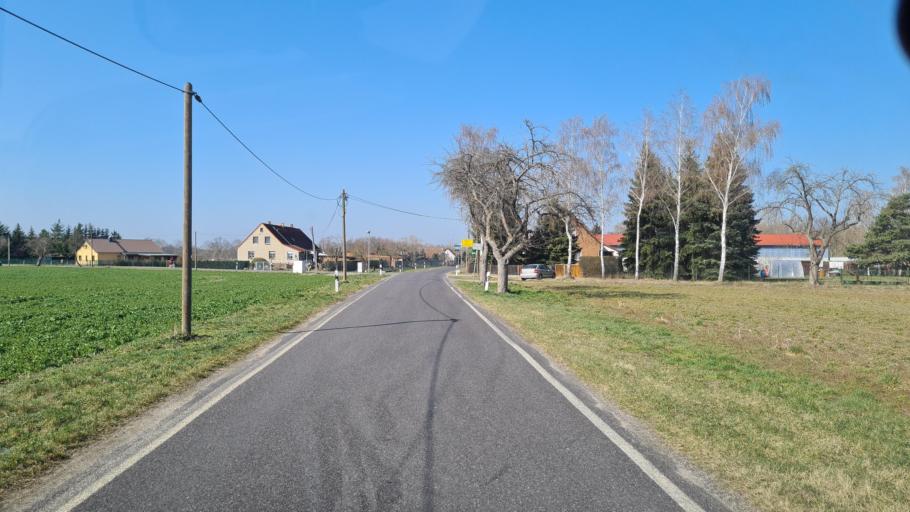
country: DE
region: Brandenburg
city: Vetschau
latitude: 51.7860
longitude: 14.0485
